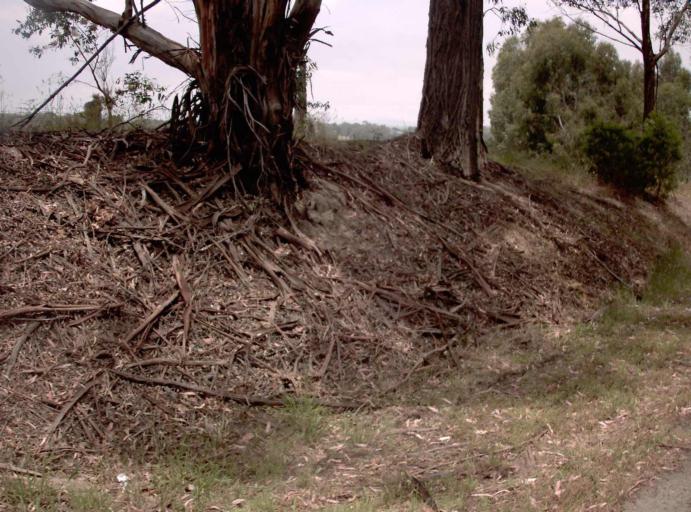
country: AU
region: Victoria
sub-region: Latrobe
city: Traralgon
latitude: -38.4606
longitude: 146.7257
